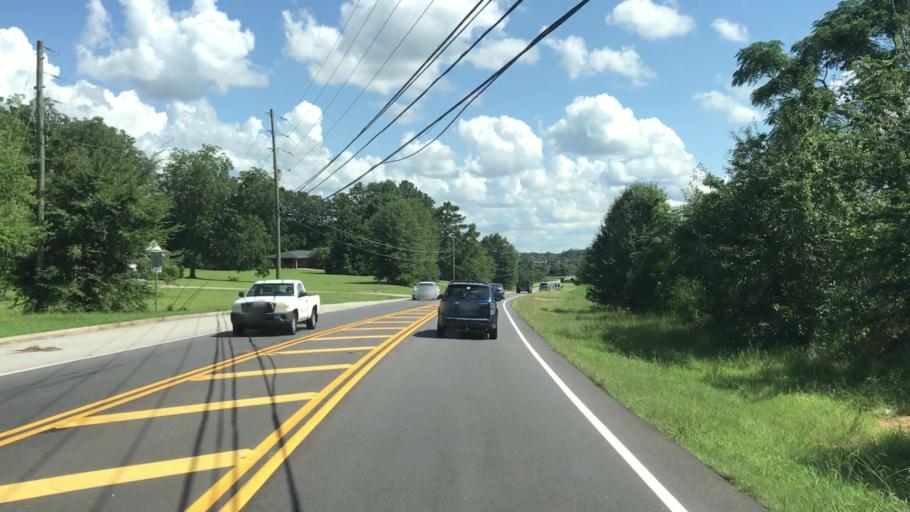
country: US
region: Georgia
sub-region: Walton County
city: Loganville
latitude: 33.8283
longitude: -83.8790
